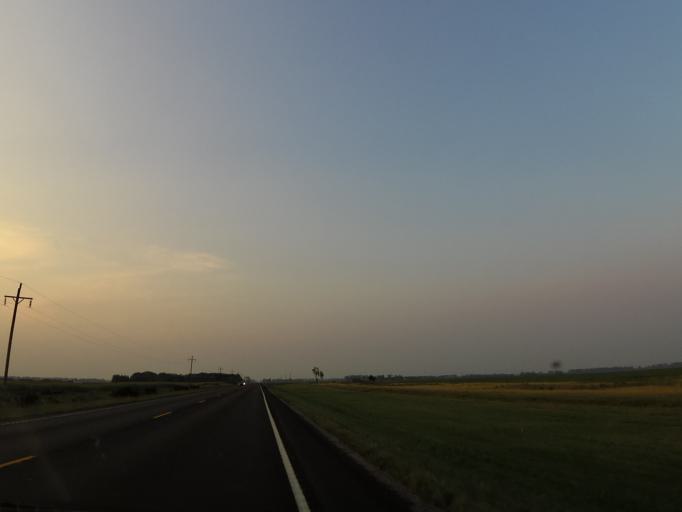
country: US
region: North Dakota
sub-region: Walsh County
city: Park River
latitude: 48.3063
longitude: -97.6223
